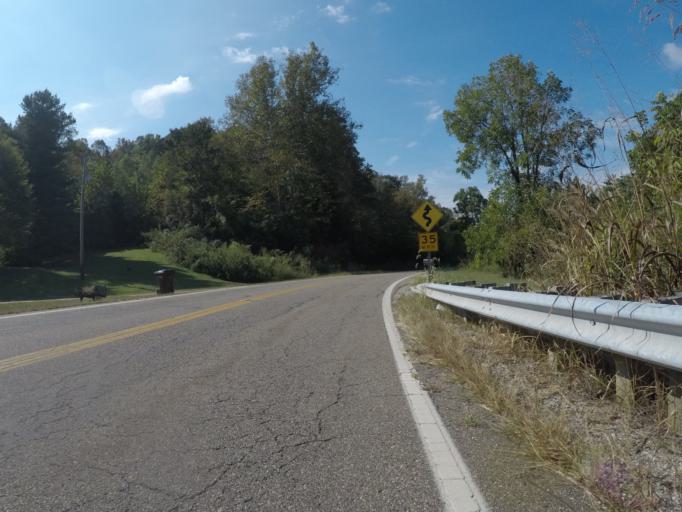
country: US
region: West Virginia
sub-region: Cabell County
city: Lesage
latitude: 38.6348
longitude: -82.4305
